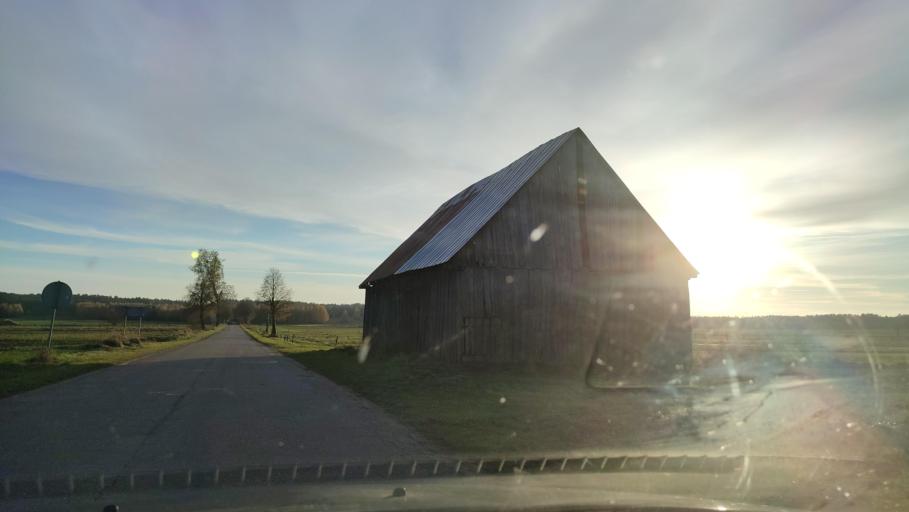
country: PL
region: Masovian Voivodeship
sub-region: Powiat mlawski
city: Dzierzgowo
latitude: 53.3085
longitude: 20.6699
